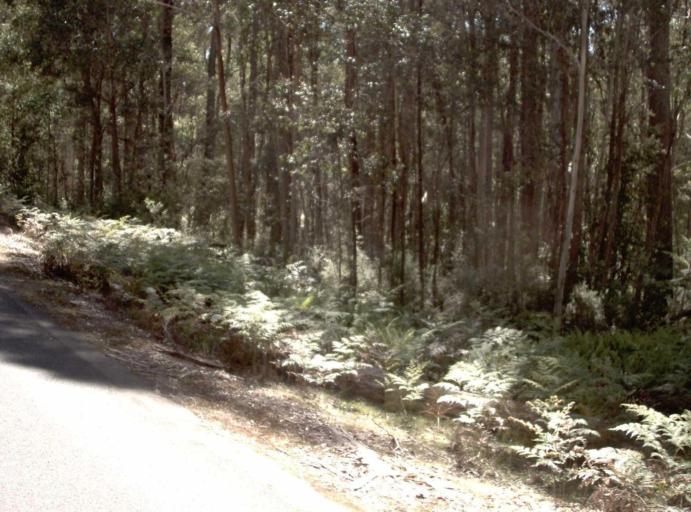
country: AU
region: New South Wales
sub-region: Bombala
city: Bombala
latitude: -37.0738
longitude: 148.7807
